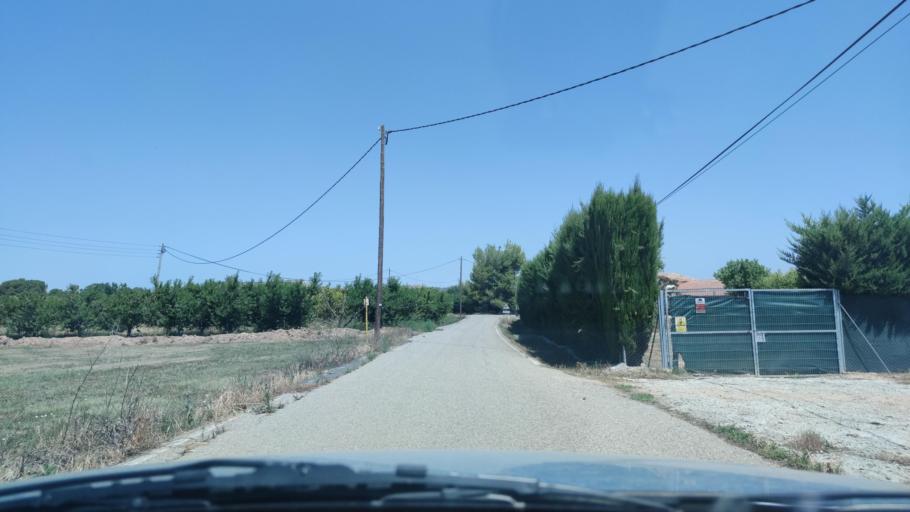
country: ES
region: Catalonia
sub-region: Provincia de Lleida
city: Torrefarrera
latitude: 41.6516
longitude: 0.5910
